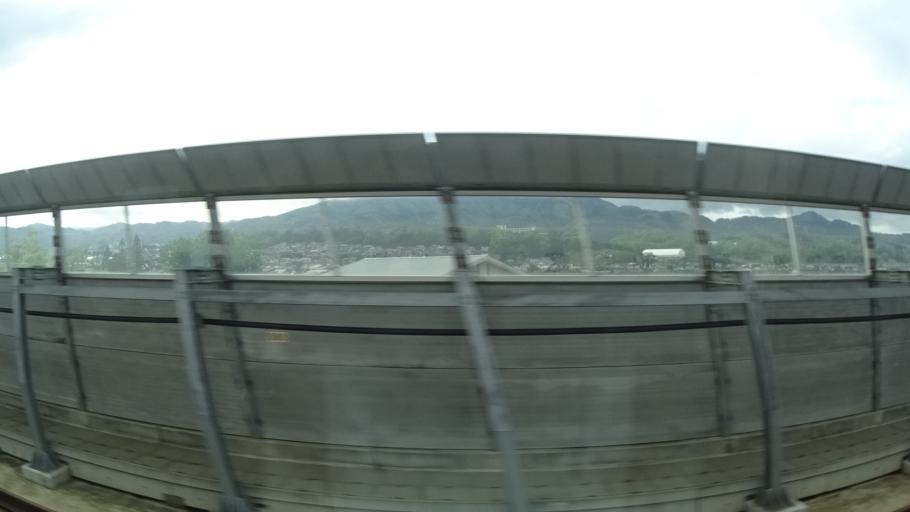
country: JP
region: Nagano
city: Suzaka
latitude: 36.6841
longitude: 138.2497
